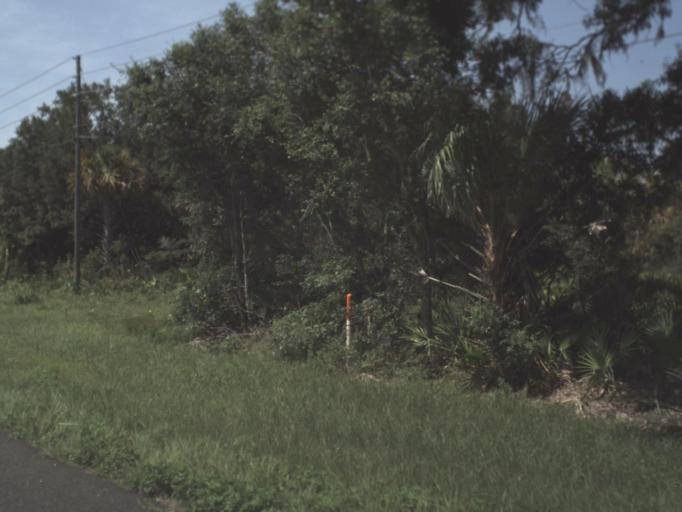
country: US
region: Florida
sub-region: Levy County
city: Inglis
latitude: 28.9724
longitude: -82.6365
